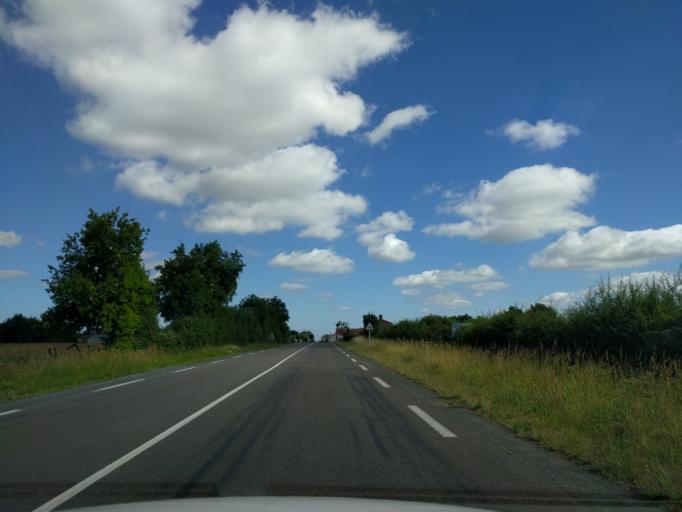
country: FR
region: Pays de la Loire
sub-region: Departement de la Vendee
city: Chantonnay
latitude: 46.6263
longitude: -1.0406
